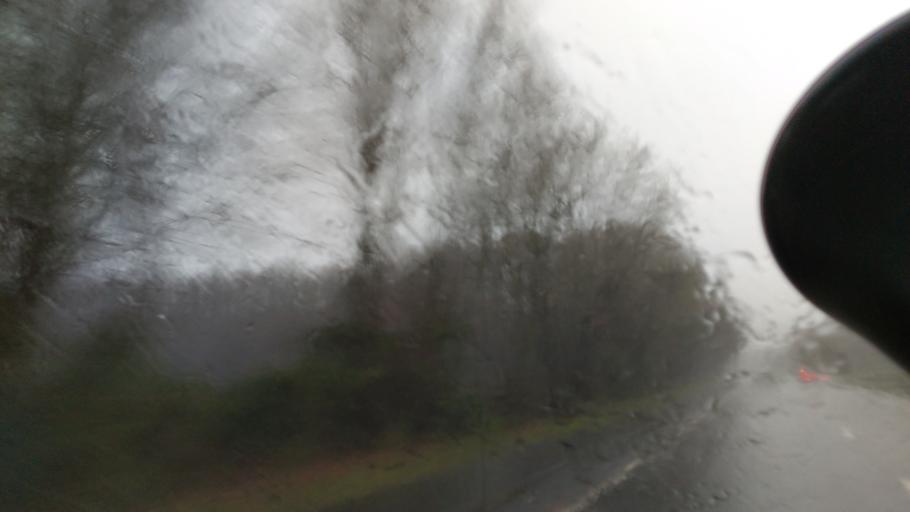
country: GB
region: England
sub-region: West Sussex
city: Walberton
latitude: 50.8576
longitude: -0.5892
